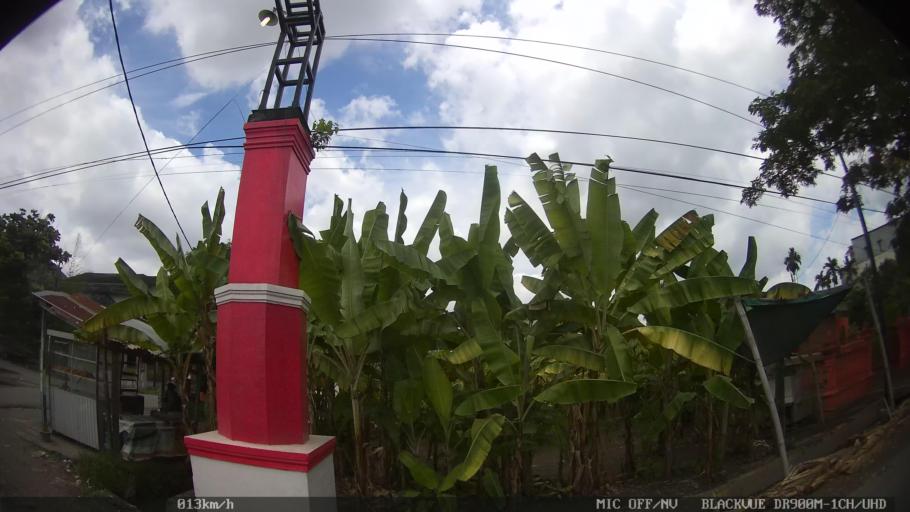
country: ID
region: North Sumatra
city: Medan
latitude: 3.6175
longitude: 98.7290
